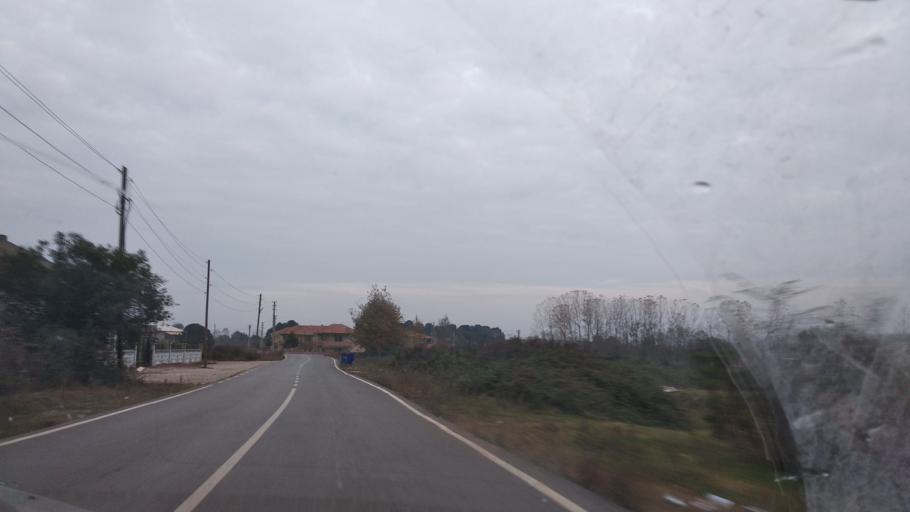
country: TR
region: Sakarya
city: Karasu
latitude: 41.0841
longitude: 30.7362
